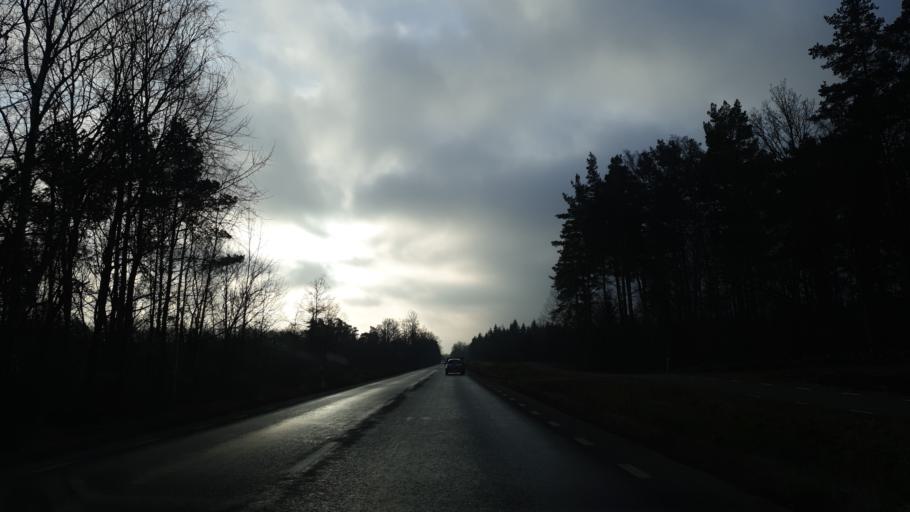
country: SE
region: Blekinge
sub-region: Karlshamns Kommun
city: Morrum
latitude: 56.1446
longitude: 14.6692
